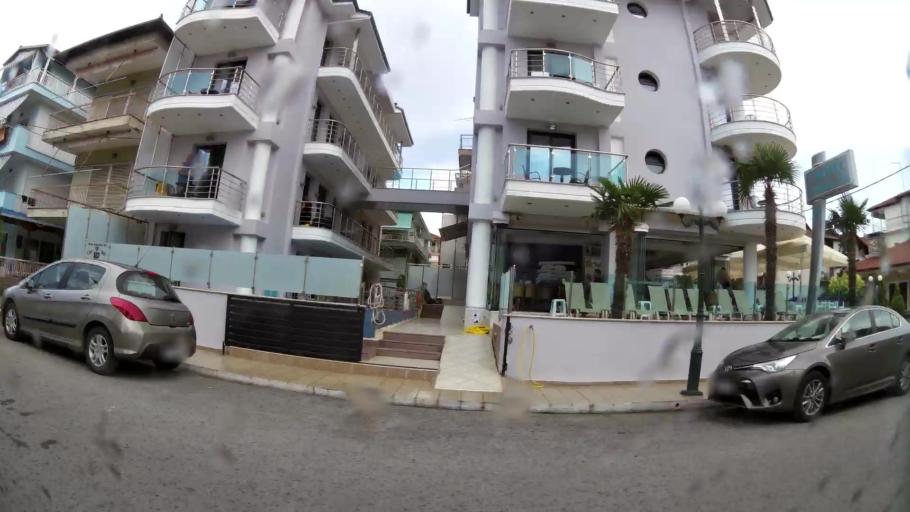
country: GR
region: Central Macedonia
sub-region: Nomos Pierias
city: Paralia
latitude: 40.2723
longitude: 22.5978
